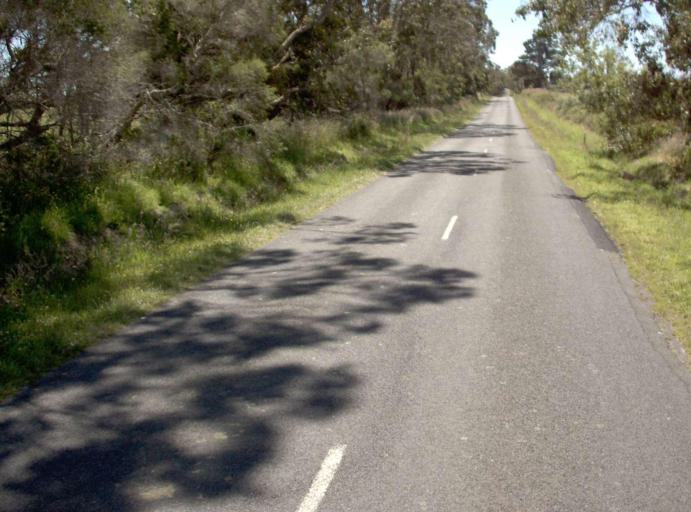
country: AU
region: Victoria
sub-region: Bass Coast
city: North Wonthaggi
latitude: -38.7818
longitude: 146.0805
